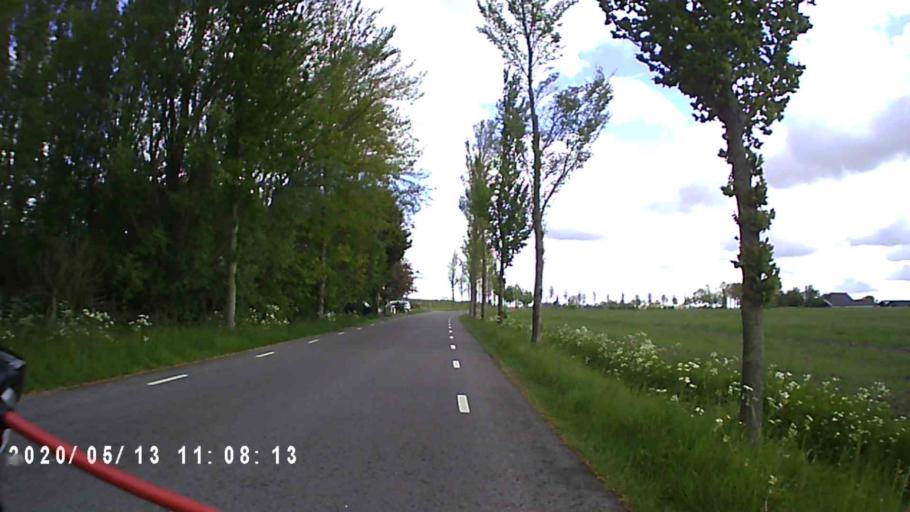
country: NL
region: Groningen
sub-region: Gemeente Zuidhorn
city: Grijpskerk
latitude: 53.2928
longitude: 6.3366
